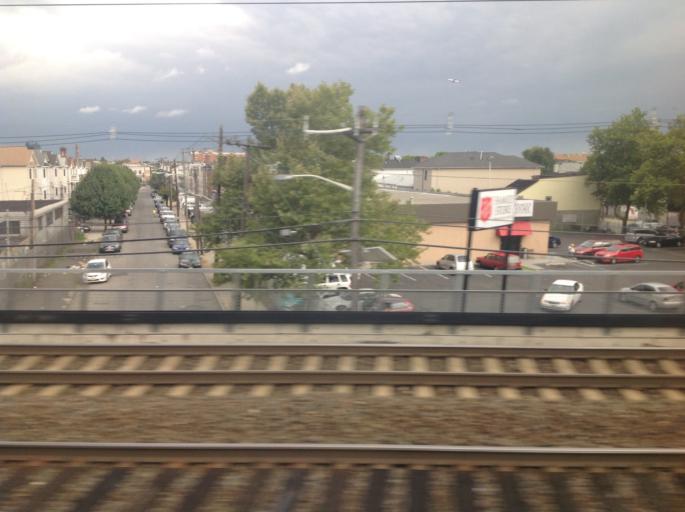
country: US
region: New Jersey
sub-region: Essex County
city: Newark
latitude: 40.7251
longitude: -74.1737
